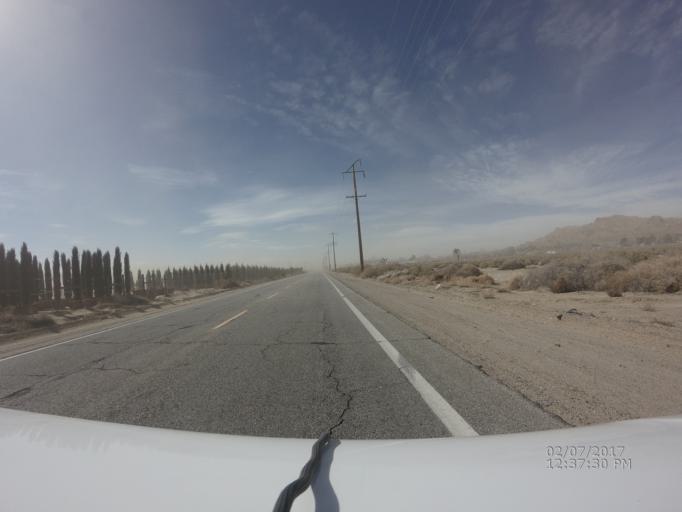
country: US
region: California
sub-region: Los Angeles County
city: Lake Los Angeles
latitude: 34.5799
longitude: -117.8420
